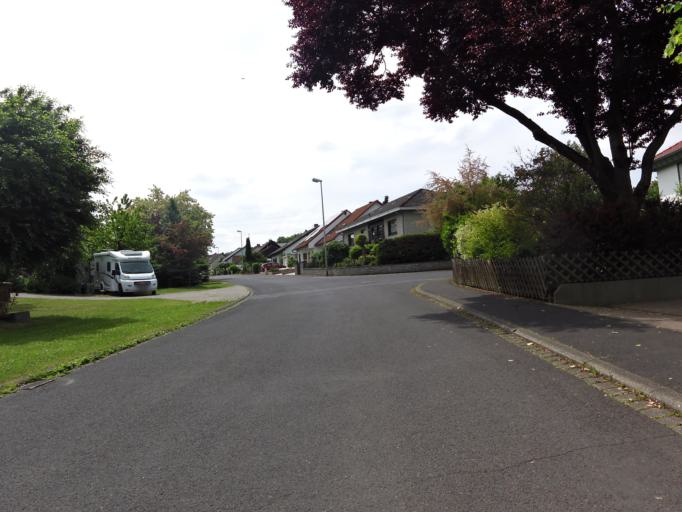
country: DE
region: Bavaria
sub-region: Regierungsbezirk Unterfranken
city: Waldbrunn
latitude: 49.7645
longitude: 9.8049
